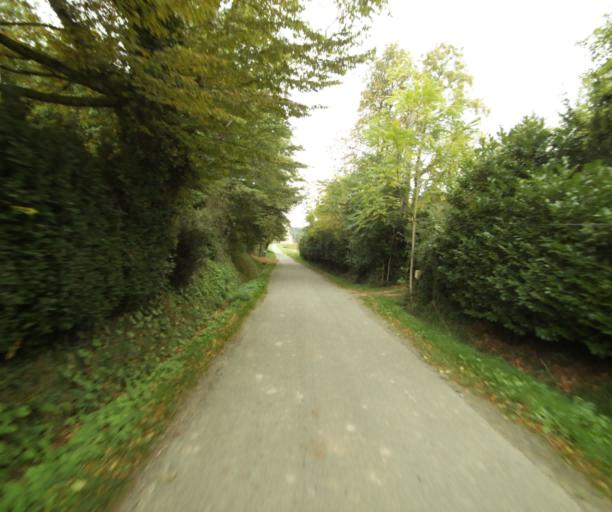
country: FR
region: Midi-Pyrenees
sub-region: Departement du Gers
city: Eauze
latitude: 43.8988
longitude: 0.0941
